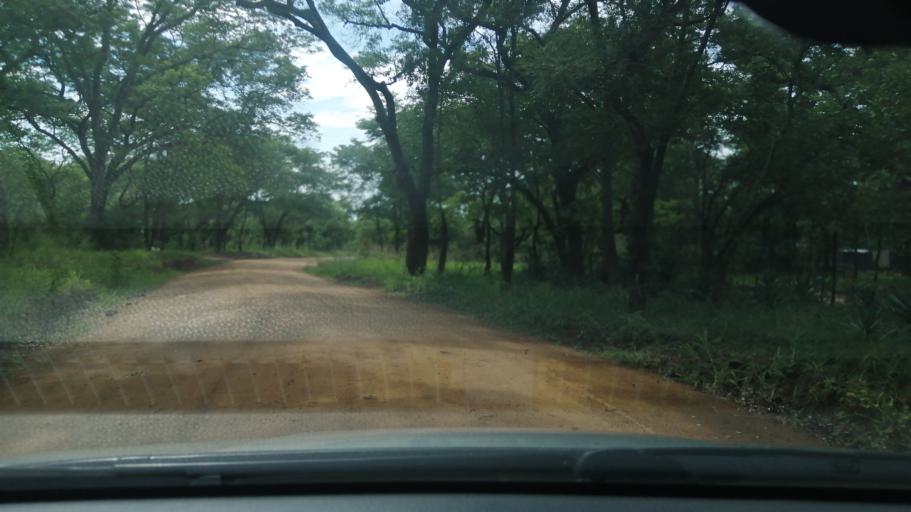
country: ZW
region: Mashonaland West
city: Norton
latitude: -17.8660
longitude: 30.8027
